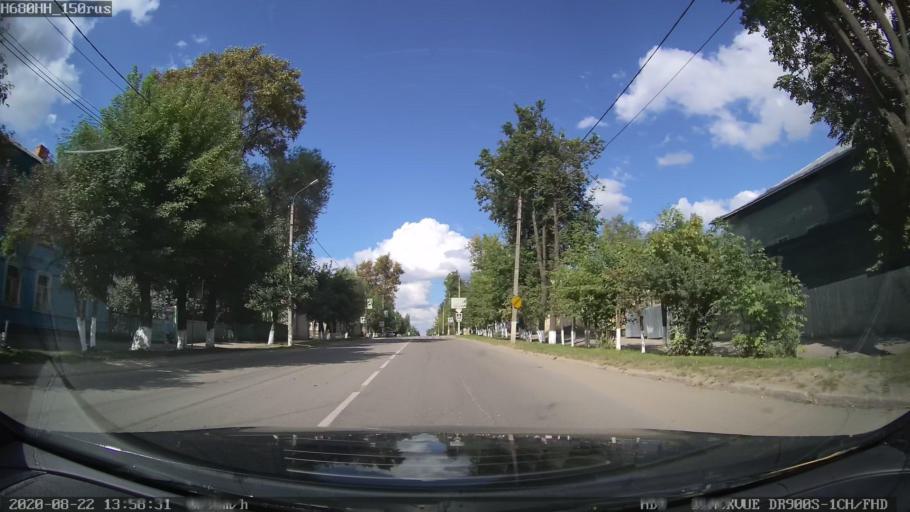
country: RU
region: Tverskaya
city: Bezhetsk
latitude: 57.7845
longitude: 36.6917
